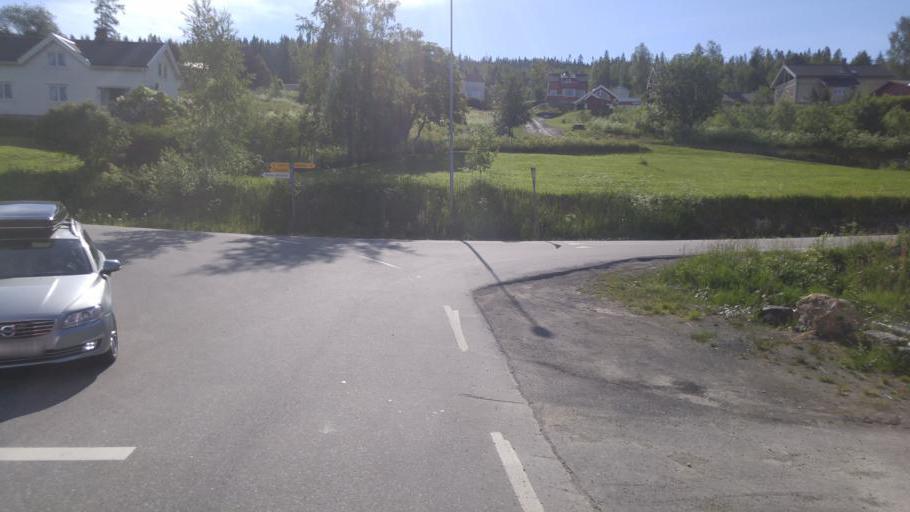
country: NO
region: Nord-Trondelag
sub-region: Meraker
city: Meraker
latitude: 63.4219
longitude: 11.7597
